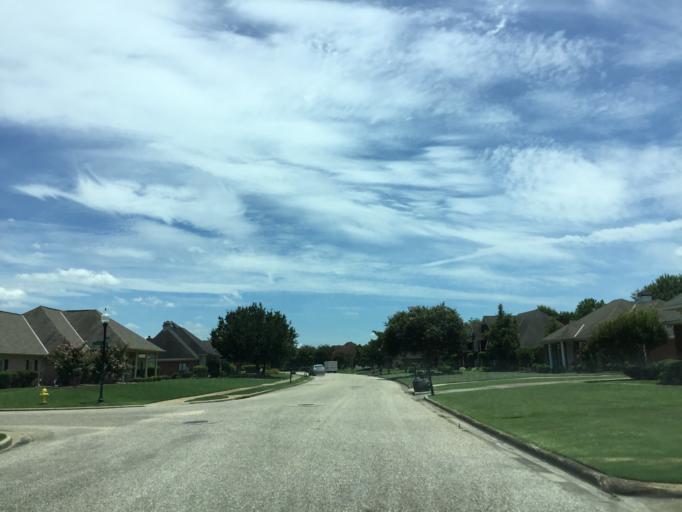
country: US
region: Alabama
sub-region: Montgomery County
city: Pike Road
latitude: 32.3799
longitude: -86.1342
